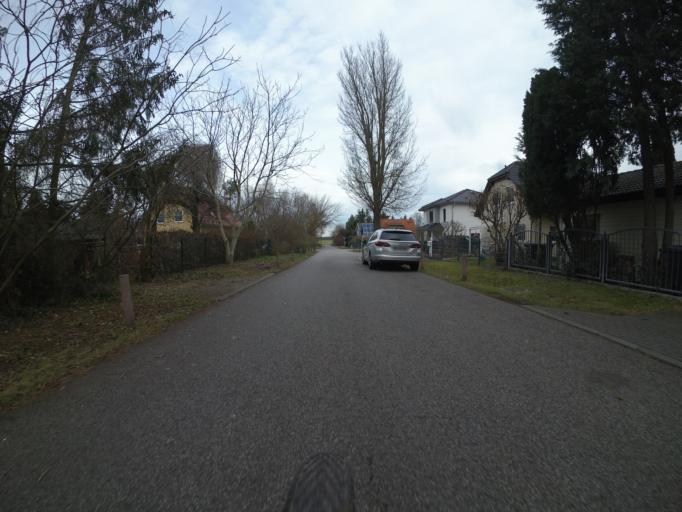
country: DE
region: Brandenburg
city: Schoneiche
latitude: 52.4713
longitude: 13.7264
